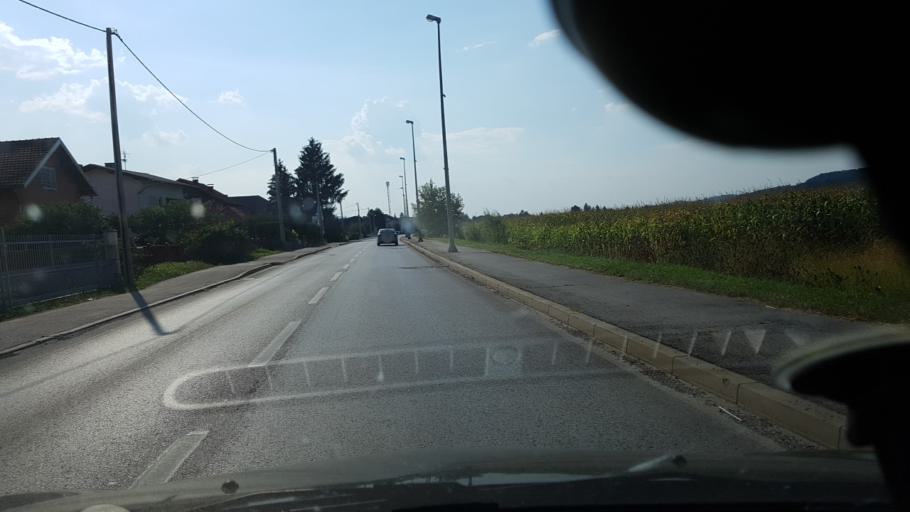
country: HR
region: Zagrebacka
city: Brdovec
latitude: 45.8608
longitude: 15.7827
